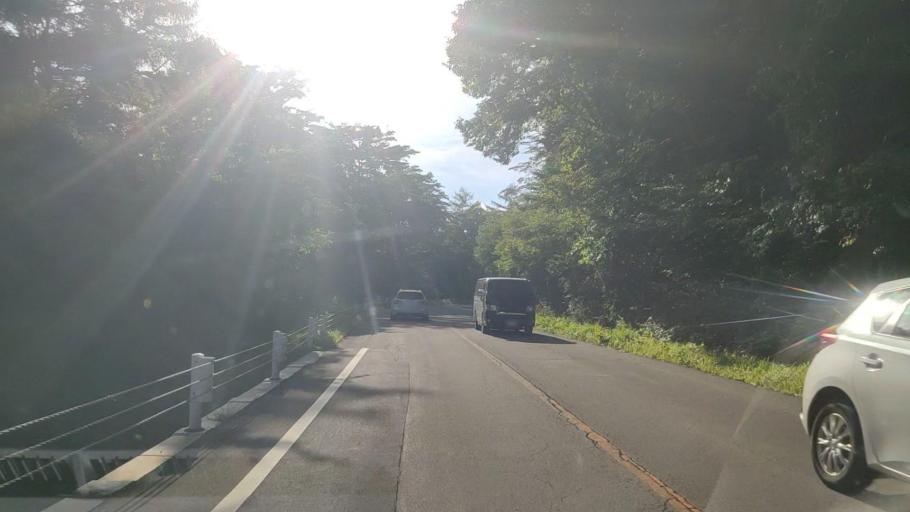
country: JP
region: Nagano
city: Ueda
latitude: 36.4888
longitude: 138.4135
